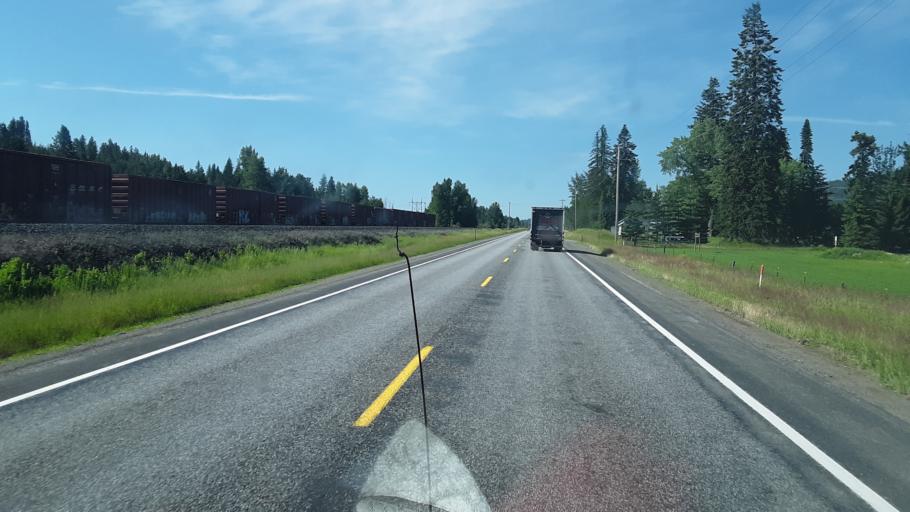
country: US
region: Idaho
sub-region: Bonner County
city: Ponderay
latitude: 48.4774
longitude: -116.4645
